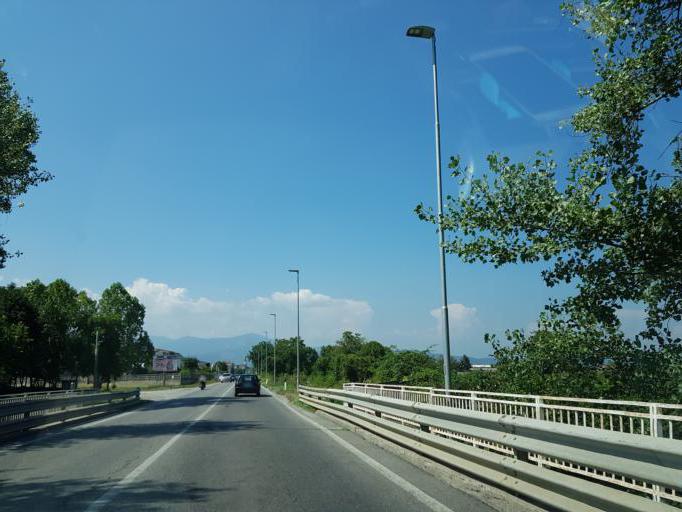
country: IT
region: Piedmont
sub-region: Provincia di Cuneo
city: Caraglio
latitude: 44.4095
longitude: 7.4412
